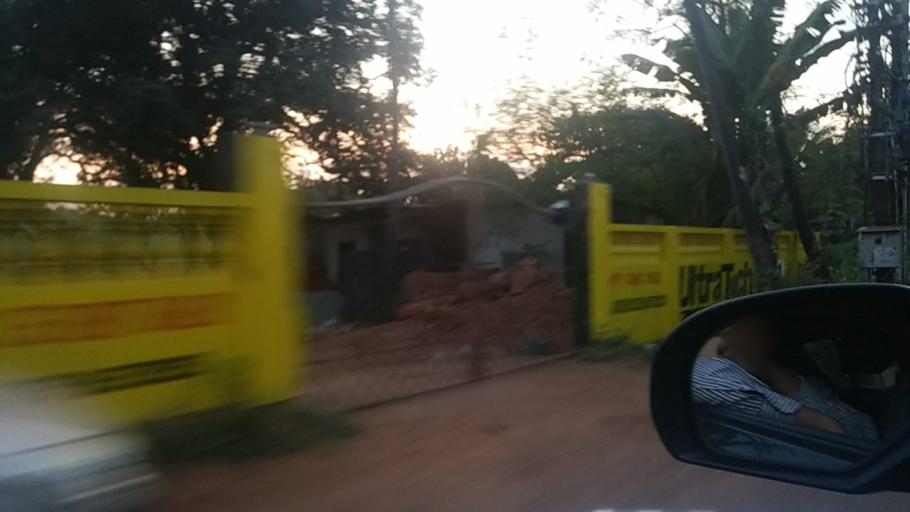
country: IN
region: Goa
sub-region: North Goa
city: Taleigao
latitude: 15.4706
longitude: 73.8441
